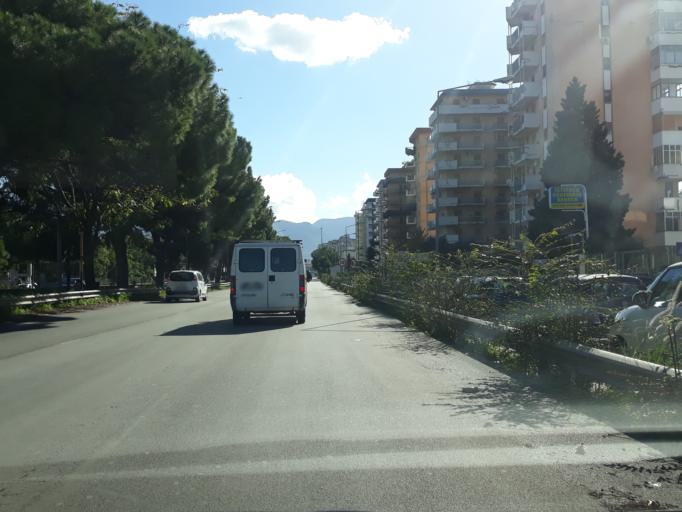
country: IT
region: Sicily
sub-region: Palermo
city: Palermo
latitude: 38.1348
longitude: 13.3304
